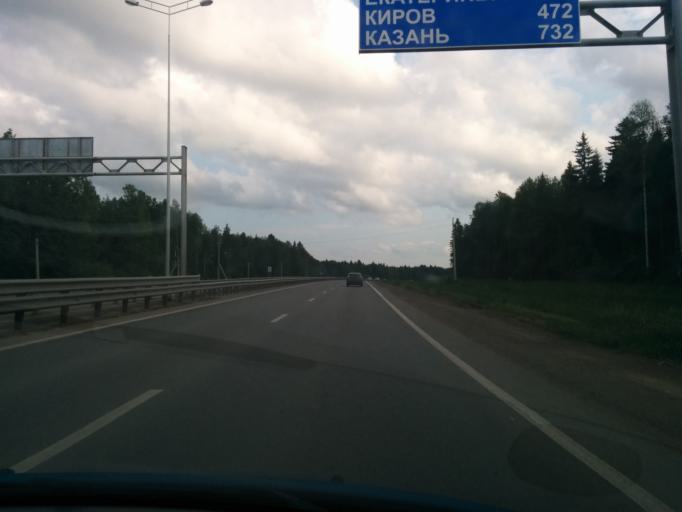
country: RU
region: Perm
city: Novyye Lyady
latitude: 58.0373
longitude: 56.4332
